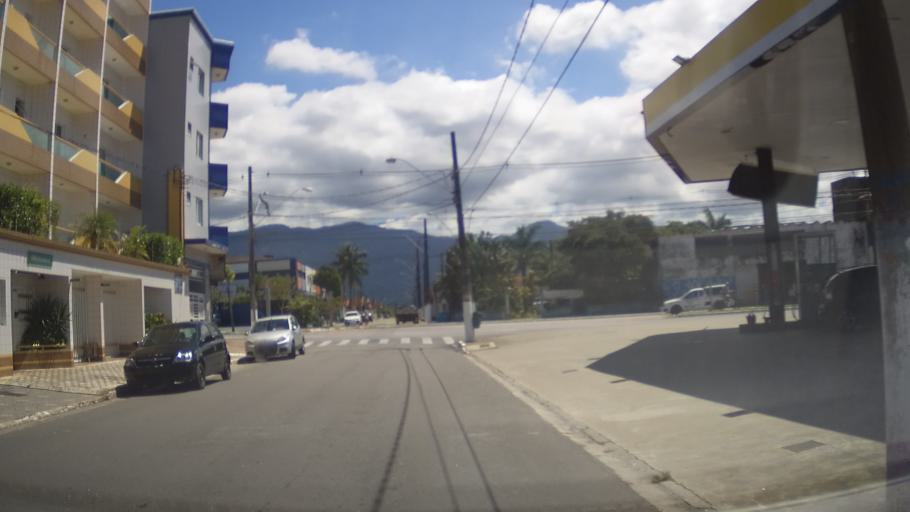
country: BR
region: Sao Paulo
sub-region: Mongagua
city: Mongagua
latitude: -24.0435
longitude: -46.5211
